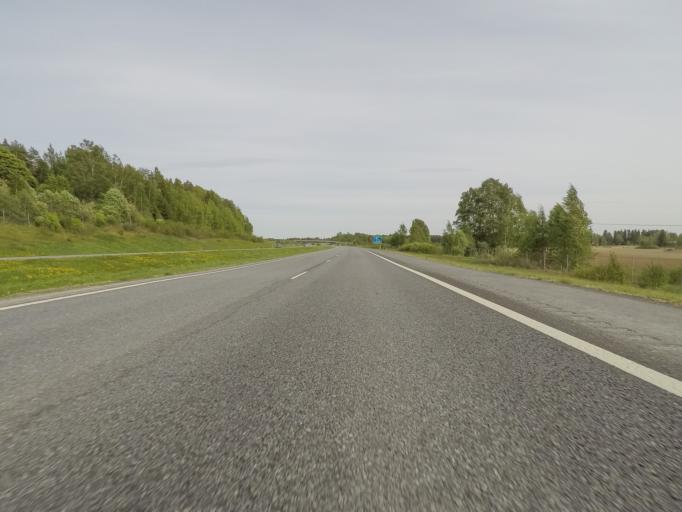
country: FI
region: Pirkanmaa
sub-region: Etelae-Pirkanmaa
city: Akaa
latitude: 61.1678
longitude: 23.9419
